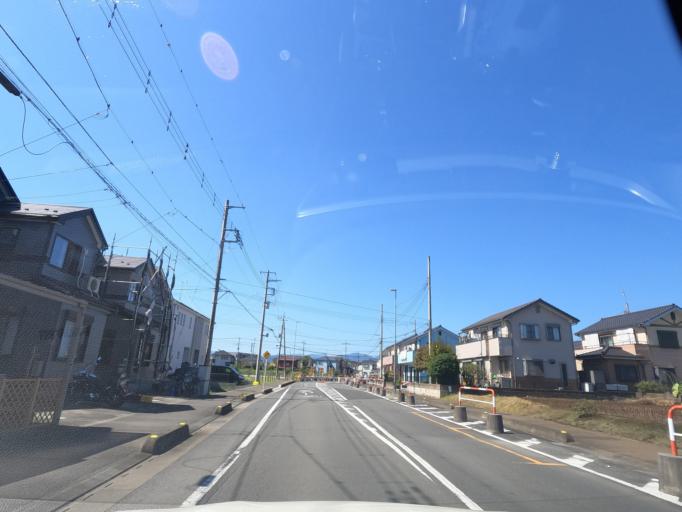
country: JP
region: Saitama
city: Hanno
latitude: 35.8501
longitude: 139.3387
